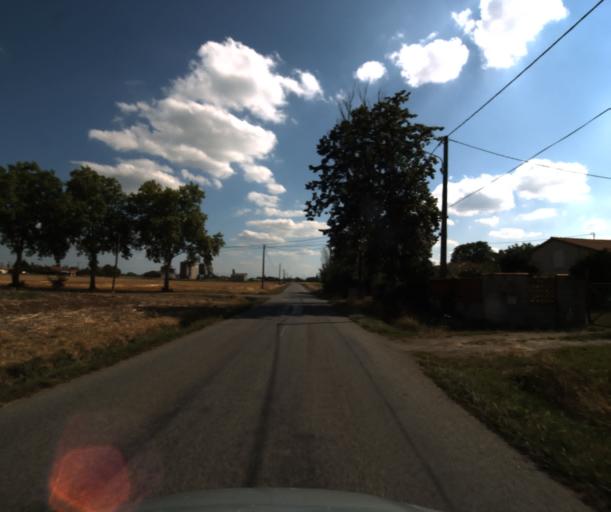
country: FR
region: Midi-Pyrenees
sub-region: Departement de la Haute-Garonne
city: Saint-Lys
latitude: 43.5275
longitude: 1.1826
